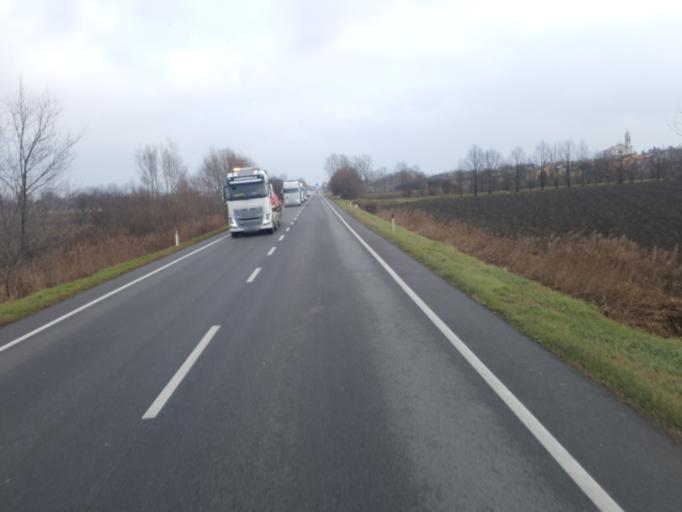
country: IT
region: Veneto
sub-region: Provincia di Padova
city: Tribano
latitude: 45.2141
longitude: 11.8211
